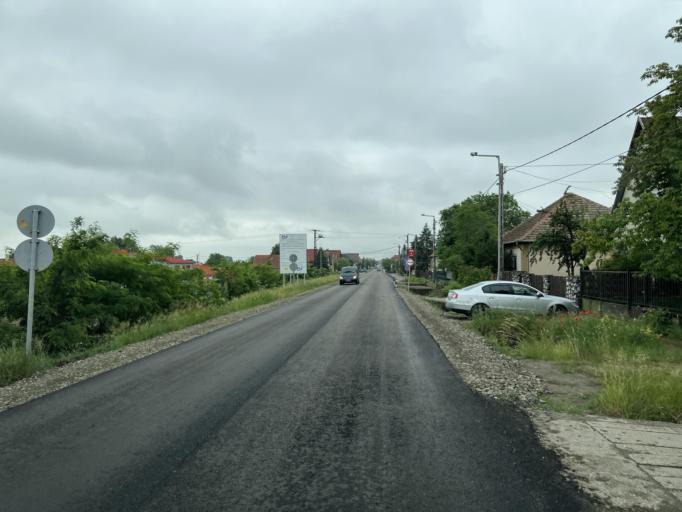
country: HU
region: Pest
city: Galgaheviz
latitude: 47.6170
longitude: 19.5760
